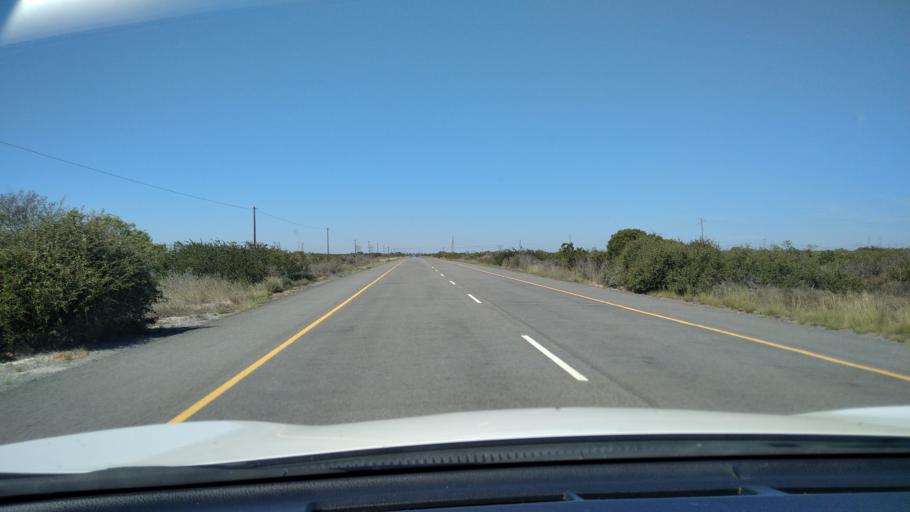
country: ZA
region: Western Cape
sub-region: West Coast District Municipality
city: Vredenburg
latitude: -33.0065
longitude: 18.2181
